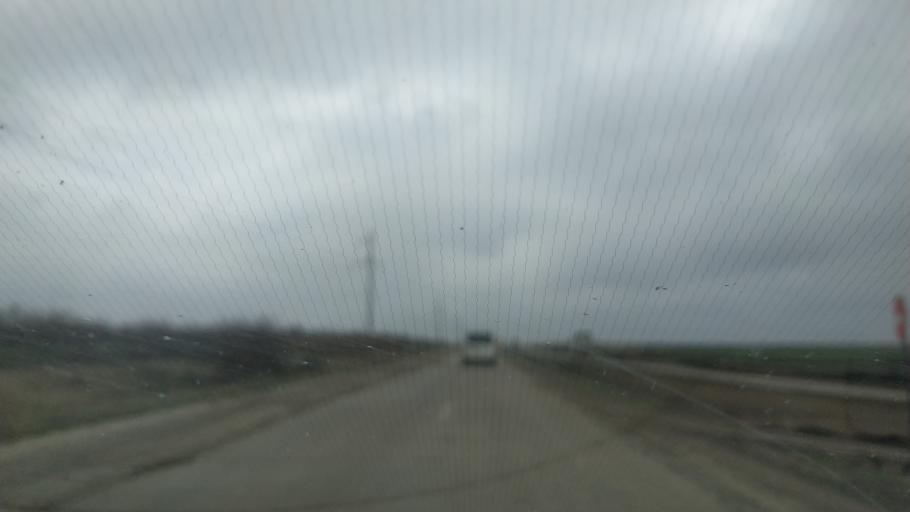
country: MD
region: Gagauzia
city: Bugeac
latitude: 46.3279
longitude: 28.7315
